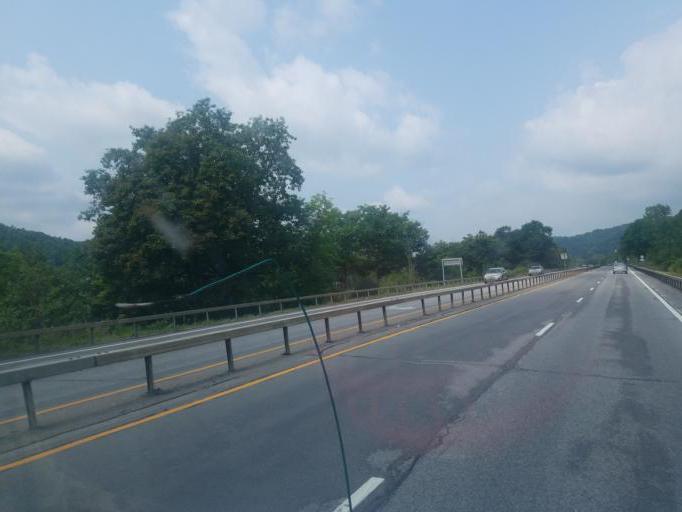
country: US
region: New York
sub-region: Herkimer County
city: Little Falls
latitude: 43.0391
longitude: -74.8400
